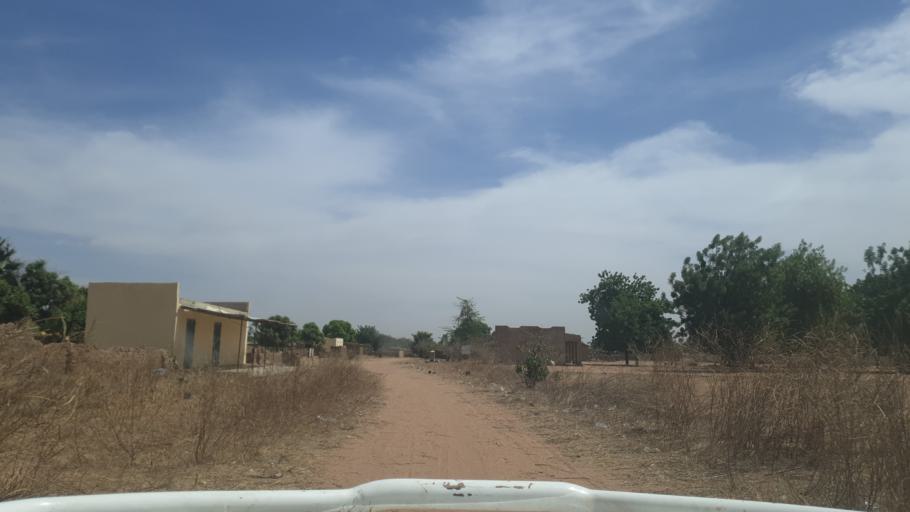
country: ML
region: Sikasso
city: Yorosso
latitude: 12.2912
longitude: -4.6549
